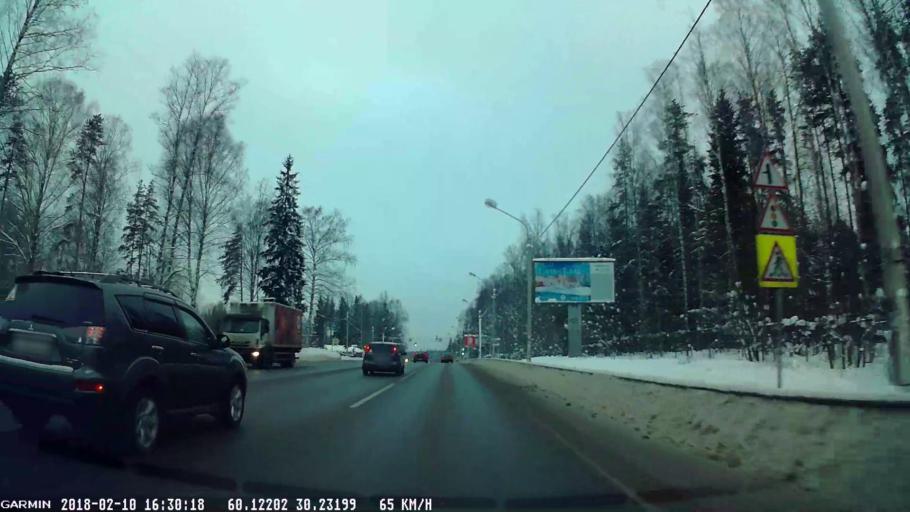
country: RU
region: St.-Petersburg
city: Levashovo
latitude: 60.1227
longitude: 30.2313
